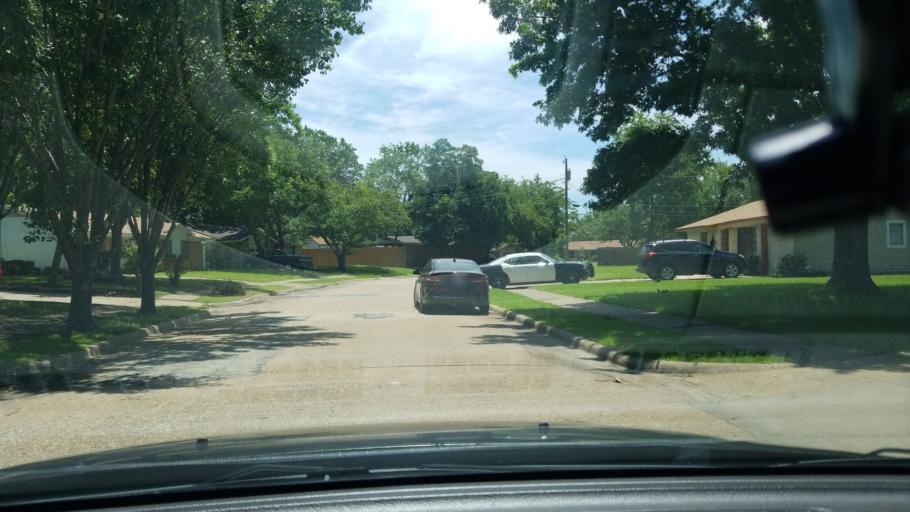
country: US
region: Texas
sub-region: Dallas County
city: Mesquite
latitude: 32.7987
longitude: -96.6551
